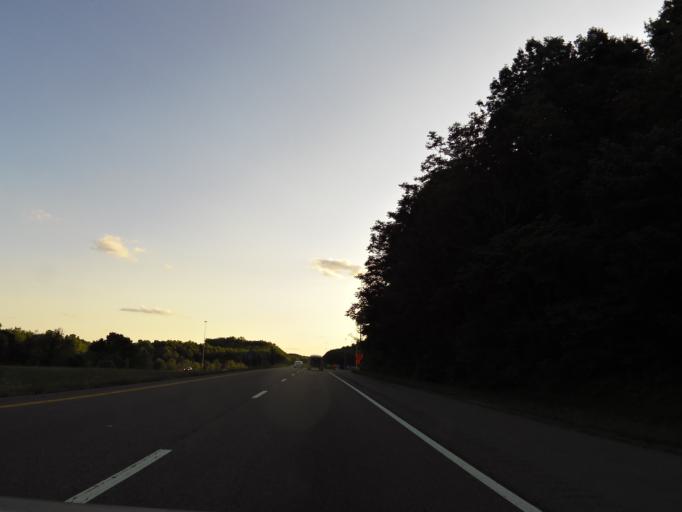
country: US
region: Tennessee
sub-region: Sullivan County
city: Blountville
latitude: 36.5470
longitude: -82.3306
